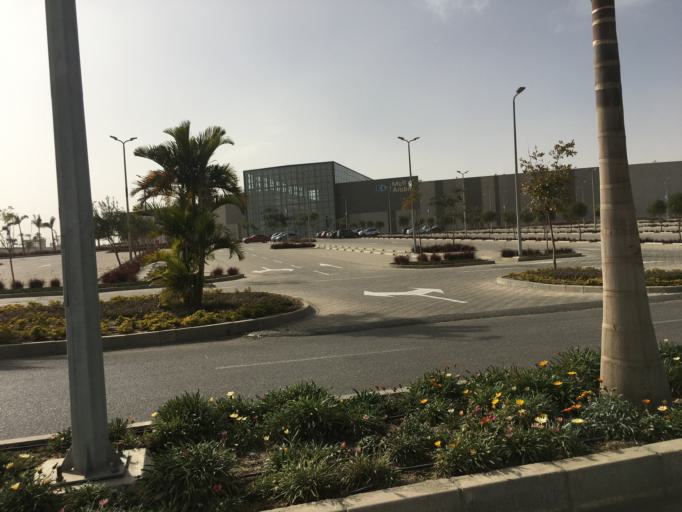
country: EG
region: Al Jizah
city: Awsim
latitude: 30.0092
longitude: 30.9801
